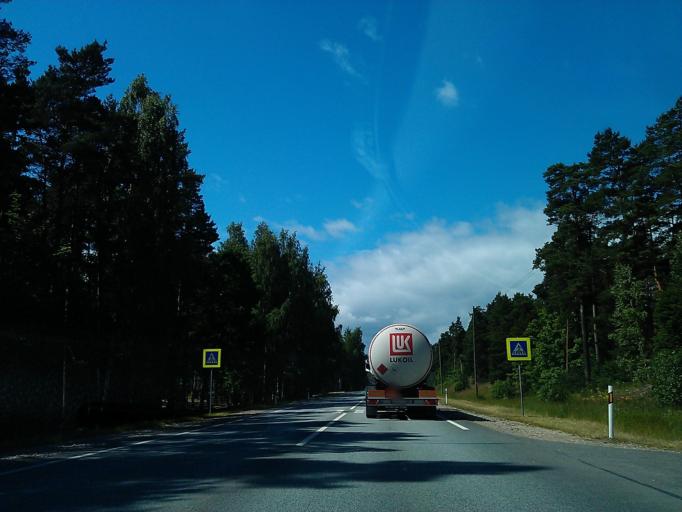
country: LV
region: Jurmala
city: Jurmala
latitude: 56.9303
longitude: 23.6940
